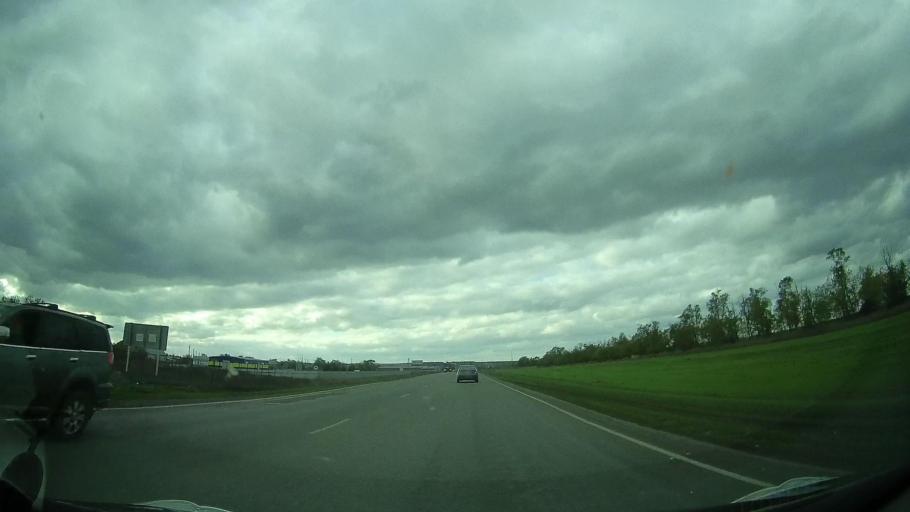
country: RU
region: Rostov
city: Kagal'nitskaya
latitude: 46.8720
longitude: 40.1655
